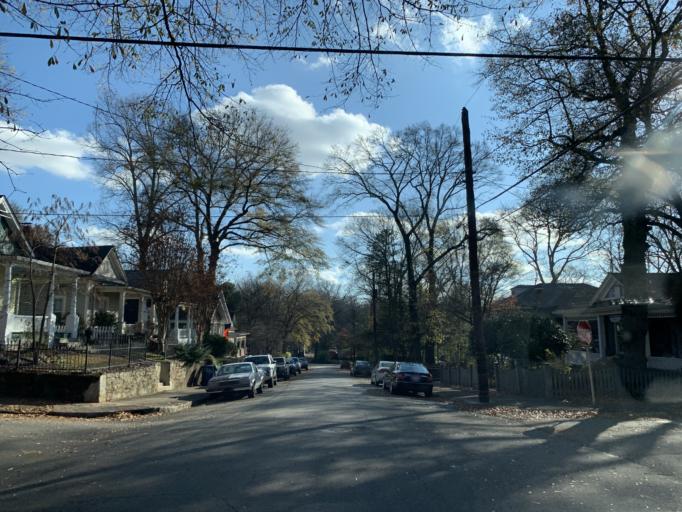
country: US
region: Georgia
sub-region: Fulton County
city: Atlanta
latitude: 33.7402
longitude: -84.3777
